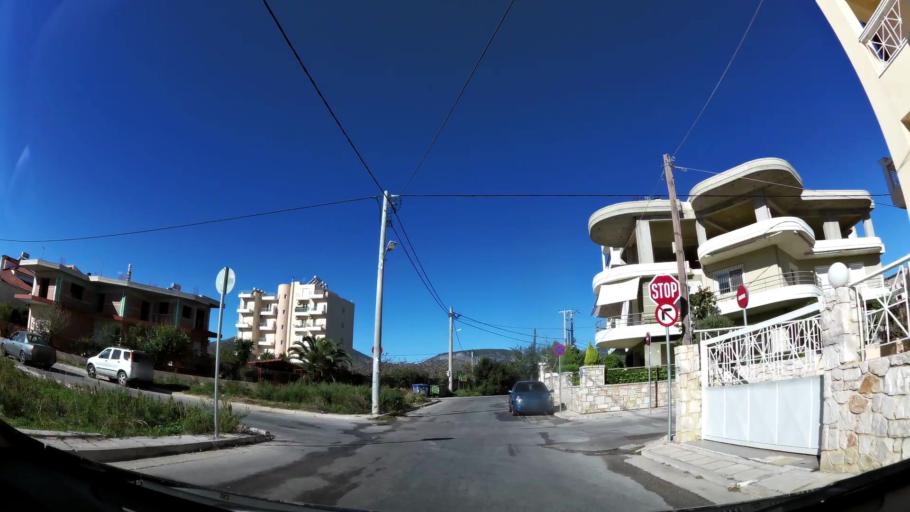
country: GR
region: Attica
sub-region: Nomarchia Anatolikis Attikis
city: Koropi
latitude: 37.9123
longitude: 23.8707
